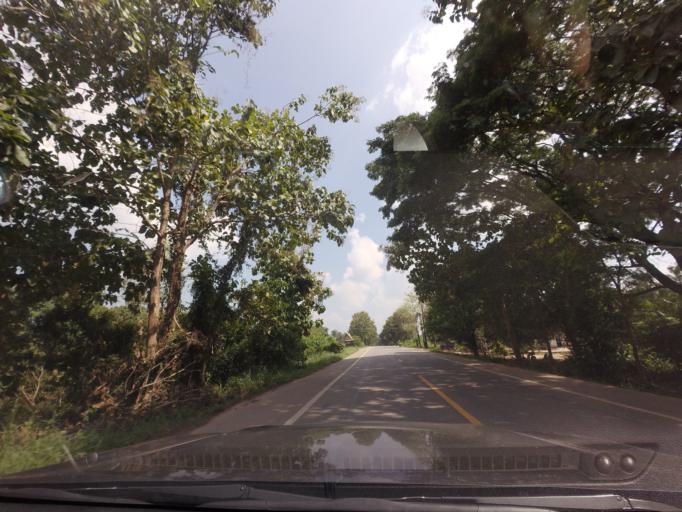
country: TH
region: Phitsanulok
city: Chat Trakan
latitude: 17.2906
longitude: 100.5153
